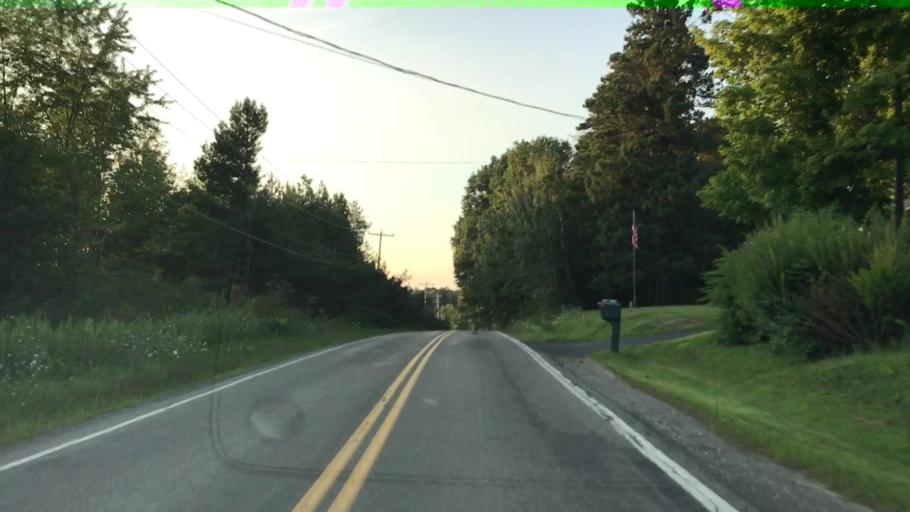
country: US
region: New York
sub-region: Chautauqua County
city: Mayville
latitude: 42.2595
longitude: -79.4691
